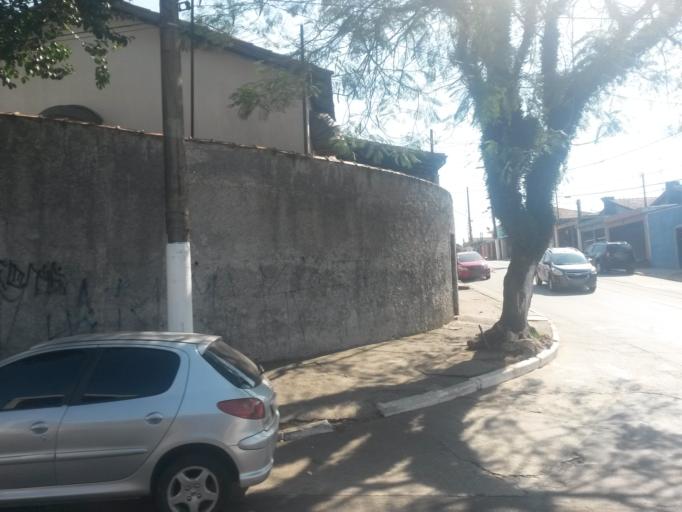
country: BR
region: Sao Paulo
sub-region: Sao Bernardo Do Campo
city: Sao Bernardo do Campo
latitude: -23.7367
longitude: -46.5365
